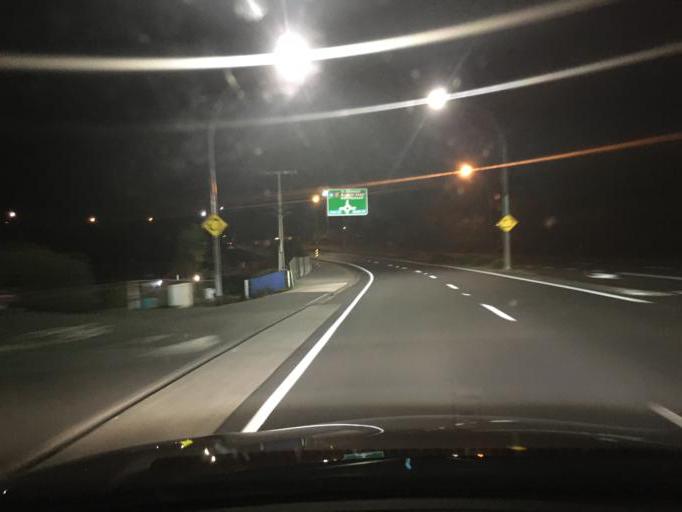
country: NZ
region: Waikato
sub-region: Hamilton City
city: Hamilton
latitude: -37.8181
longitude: 175.2821
